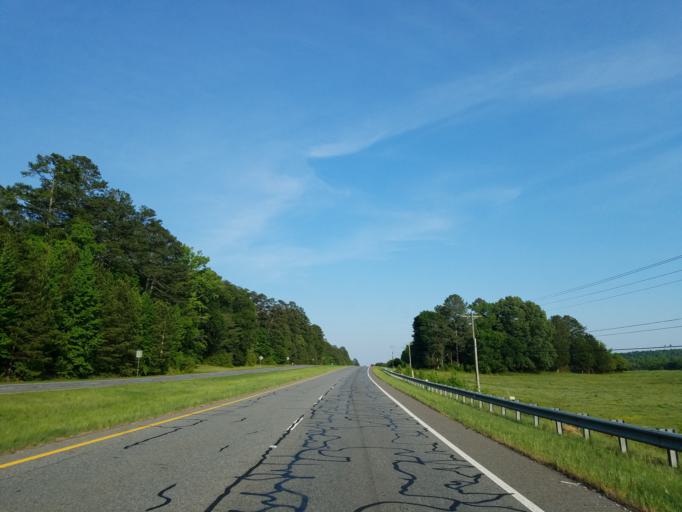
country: US
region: Georgia
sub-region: Chattooga County
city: Summerville
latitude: 34.4188
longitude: -85.2405
